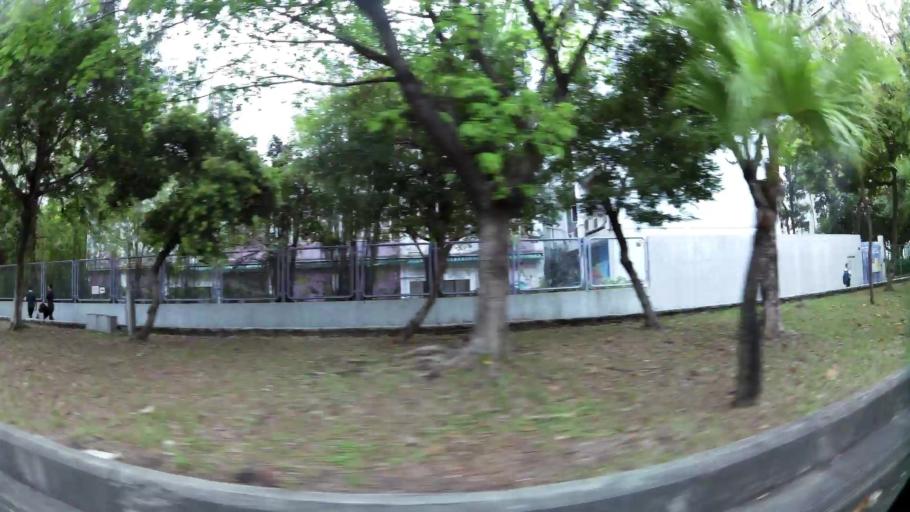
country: HK
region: Yuen Long
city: Yuen Long Kau Hui
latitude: 22.4537
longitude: 114.0036
